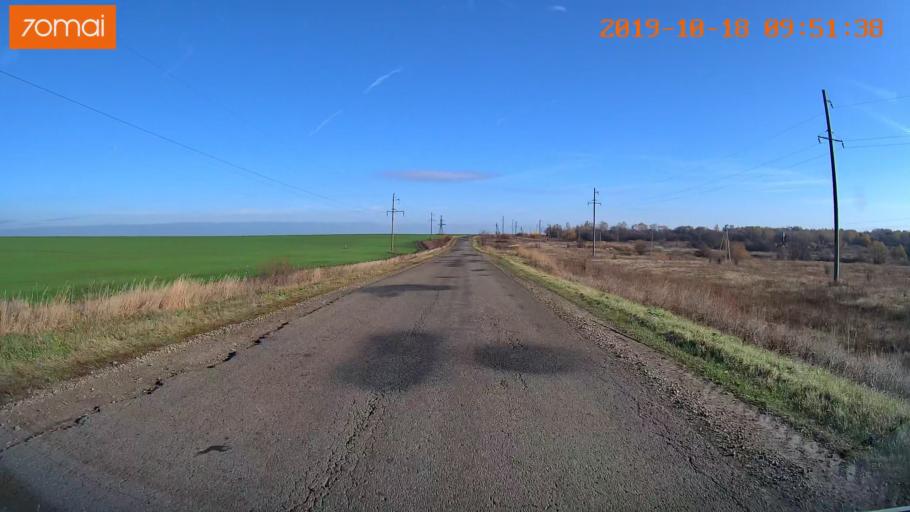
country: RU
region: Tula
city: Kazachka
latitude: 53.3432
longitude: 38.2957
